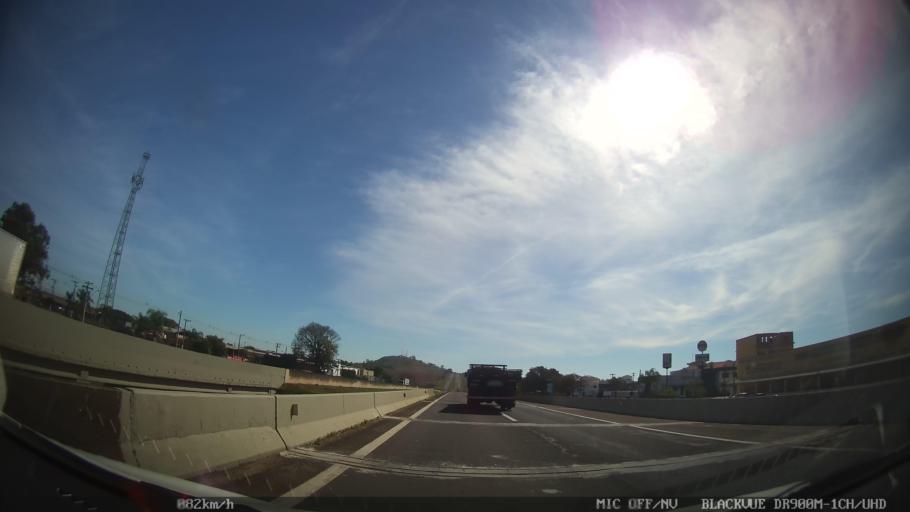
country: BR
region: Sao Paulo
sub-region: Leme
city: Leme
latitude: -22.1756
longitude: -47.3988
